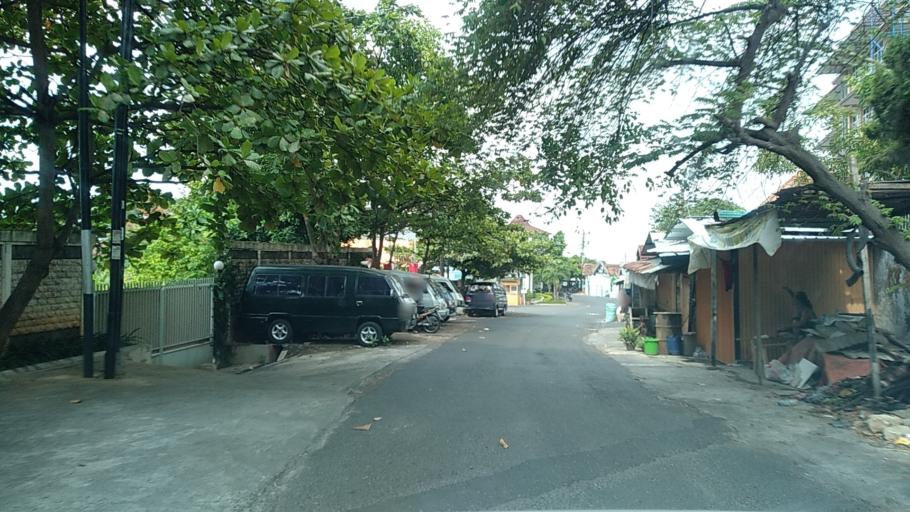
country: ID
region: Central Java
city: Semarang
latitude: -7.0067
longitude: 110.4197
